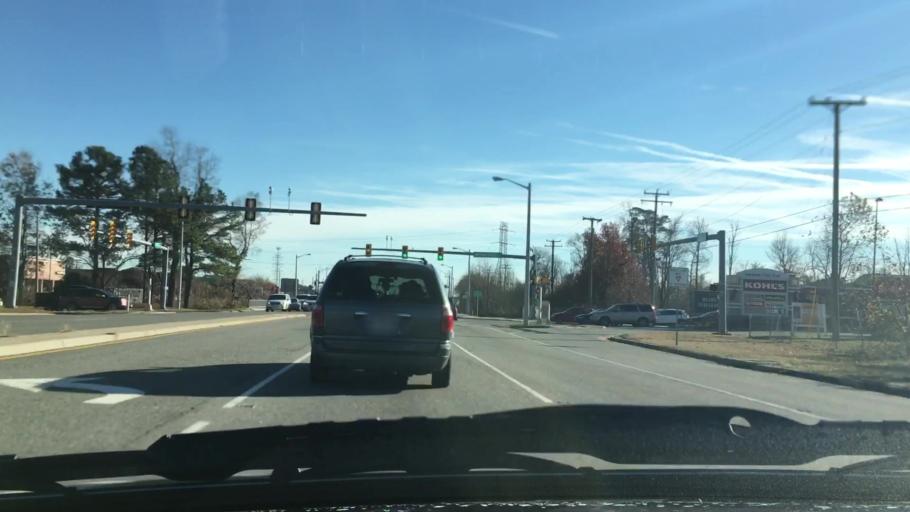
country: US
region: Virginia
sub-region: City of Portsmouth
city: Portsmouth Heights
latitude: 36.8820
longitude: -76.4259
